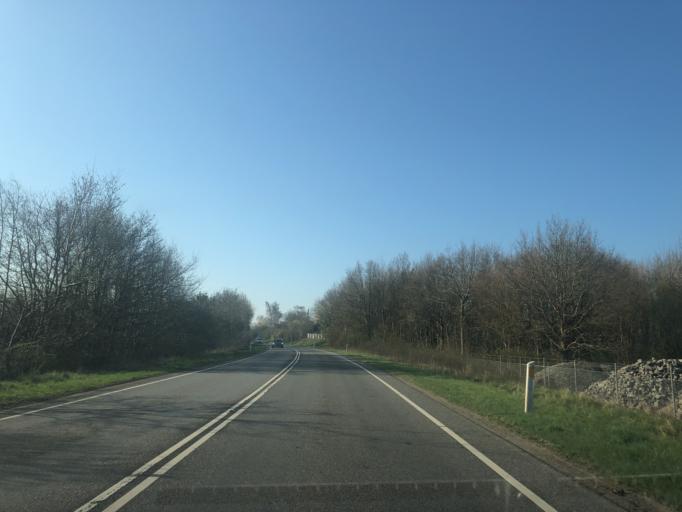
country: DK
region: Zealand
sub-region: Faxe Kommune
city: Haslev
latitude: 55.3265
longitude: 11.9410
